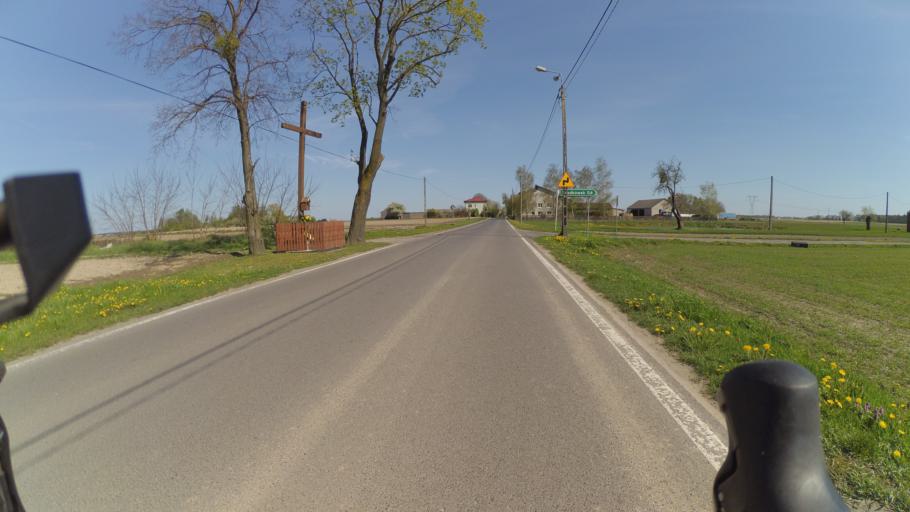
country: PL
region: Masovian Voivodeship
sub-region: Powiat warszawski zachodni
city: Leszno
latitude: 52.2453
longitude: 20.5427
